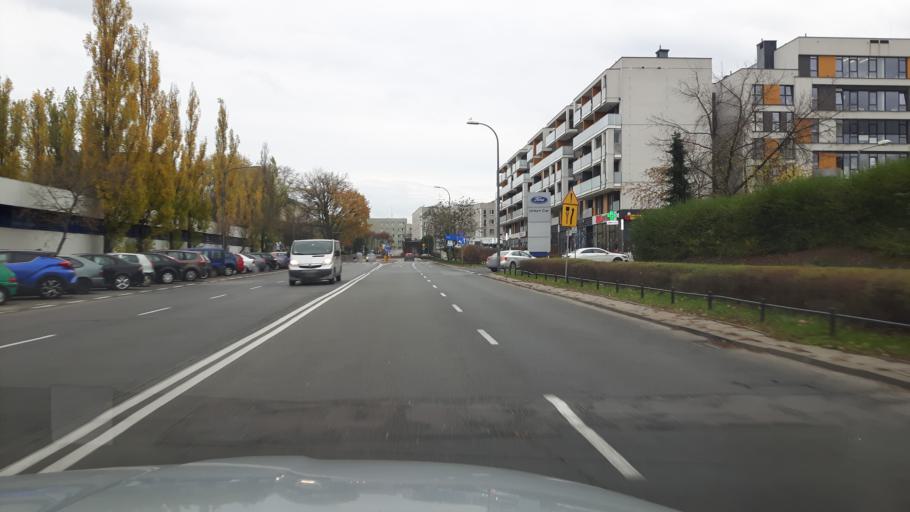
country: PL
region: Masovian Voivodeship
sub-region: Warszawa
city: Ursynow
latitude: 52.1574
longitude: 21.0213
